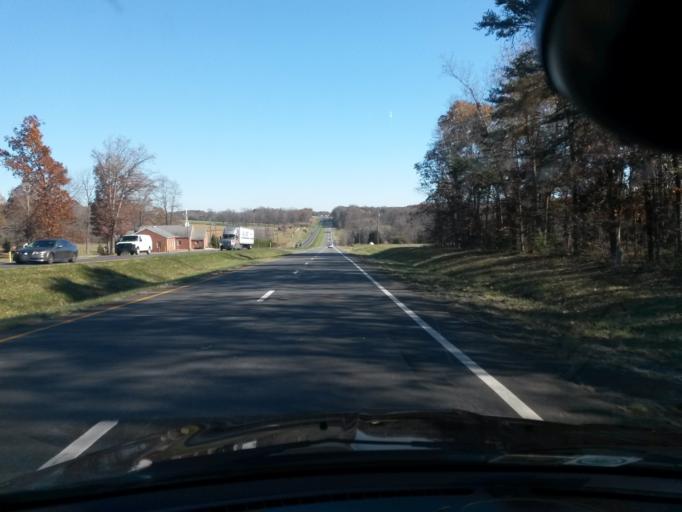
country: US
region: Virginia
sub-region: Bedford County
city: Forest
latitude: 37.3021
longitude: -79.3300
